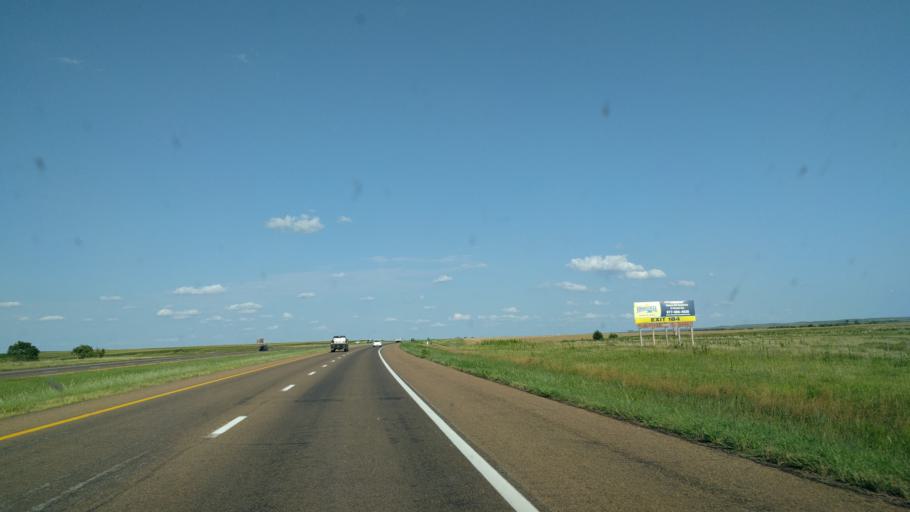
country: US
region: Kansas
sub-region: Ellis County
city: Ellis
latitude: 38.9493
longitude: -99.5242
